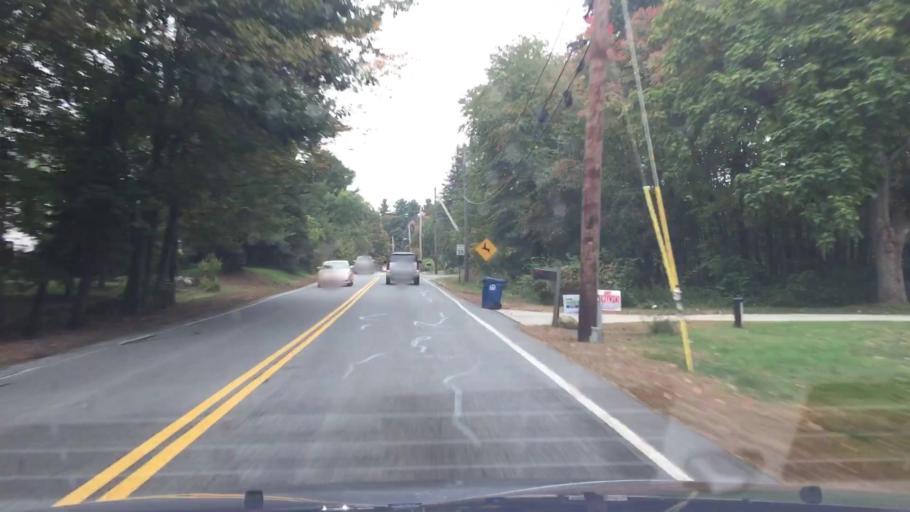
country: US
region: Massachusetts
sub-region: Middlesex County
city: Tyngsboro
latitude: 42.6989
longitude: -71.3881
